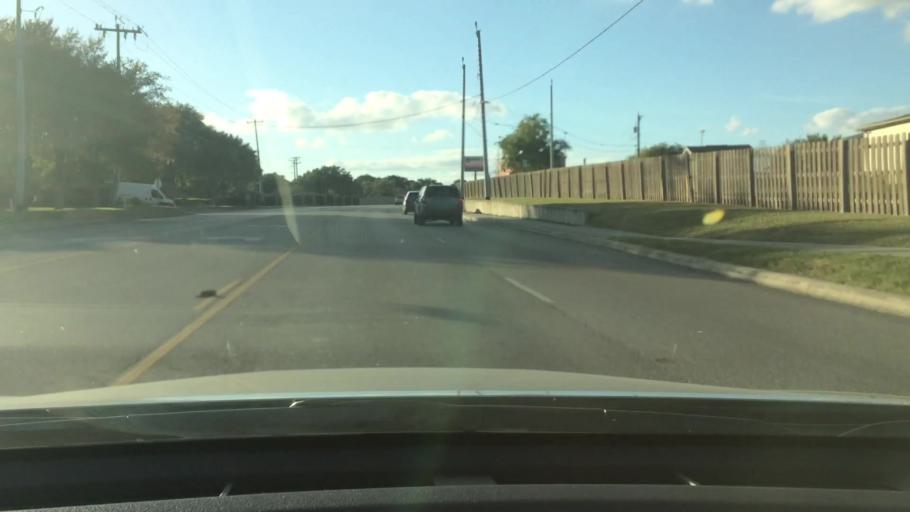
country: US
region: Texas
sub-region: Bexar County
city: Converse
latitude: 29.5209
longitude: -98.3419
